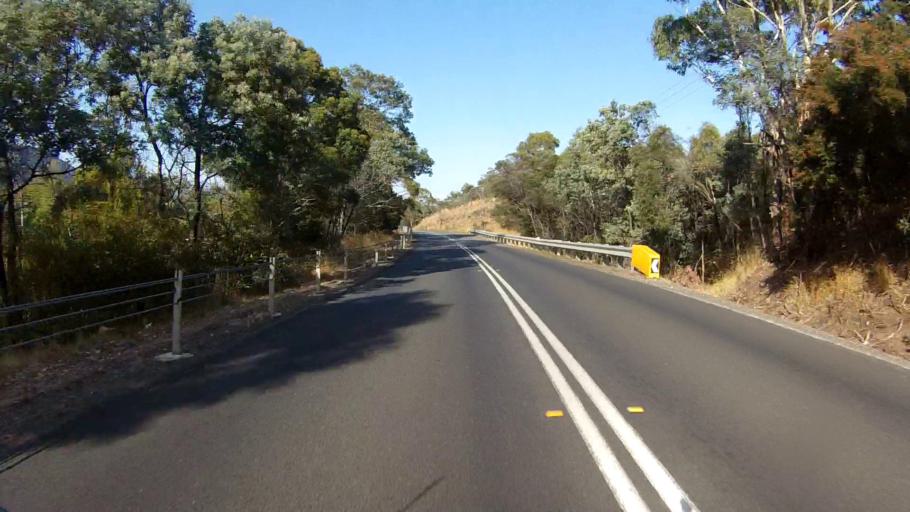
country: AU
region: Tasmania
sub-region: Derwent Valley
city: New Norfolk
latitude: -42.7573
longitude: 147.1410
